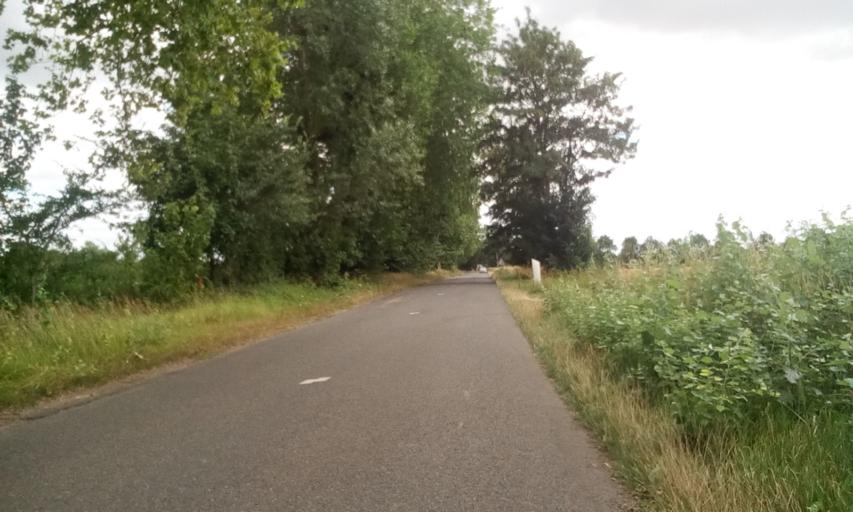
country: FR
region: Lower Normandy
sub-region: Departement du Calvados
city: Bellengreville
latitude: 49.1408
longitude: -0.2061
